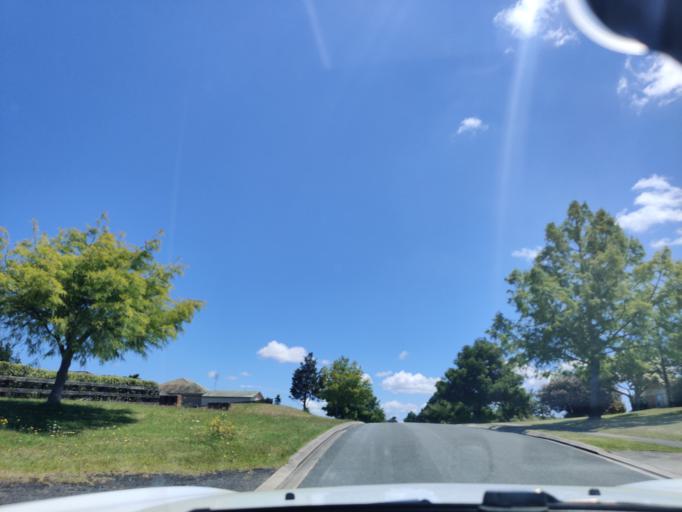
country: NZ
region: Waikato
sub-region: Waikato District
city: Te Kauwhata
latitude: -37.4043
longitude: 175.1526
